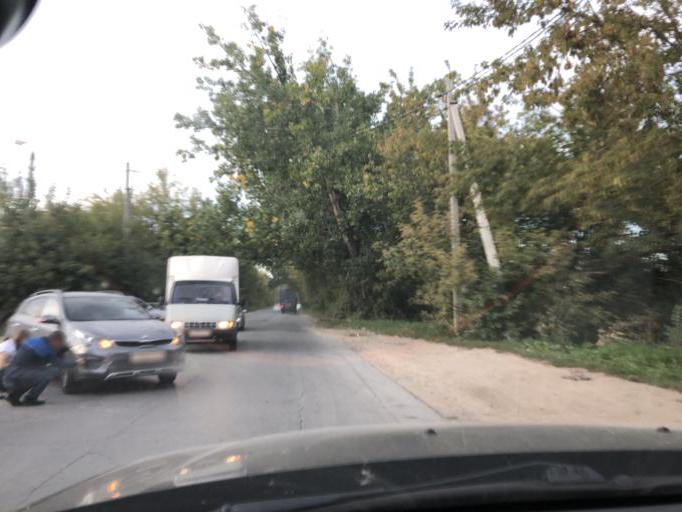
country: RU
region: Tula
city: Tula
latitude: 54.1608
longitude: 37.6171
